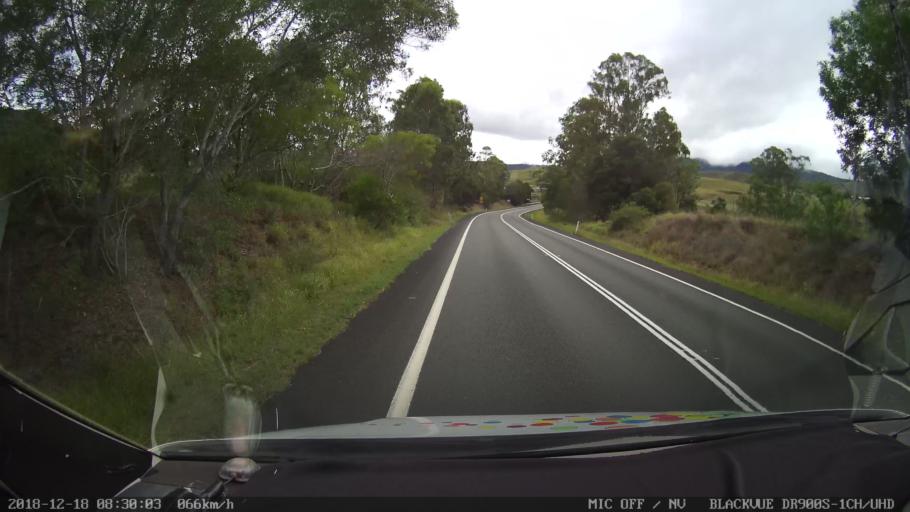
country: AU
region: New South Wales
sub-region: Kyogle
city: Kyogle
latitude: -28.3232
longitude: 152.7650
